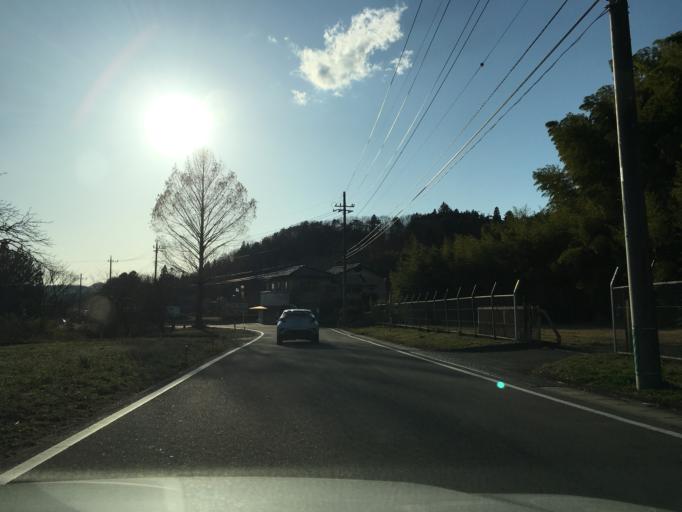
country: JP
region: Ibaraki
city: Daigo
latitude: 36.7753
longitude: 140.2450
